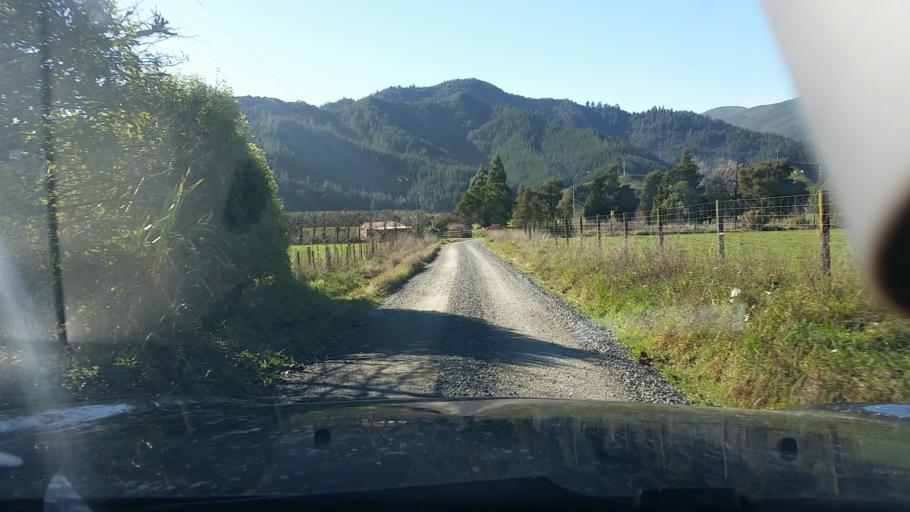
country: NZ
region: Marlborough
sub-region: Marlborough District
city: Blenheim
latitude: -41.4313
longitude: 173.7633
